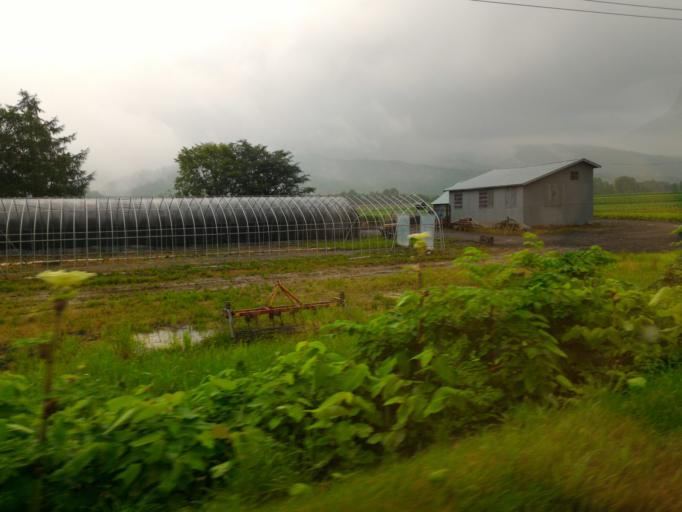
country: JP
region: Hokkaido
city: Nayoro
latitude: 44.5884
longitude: 142.3059
